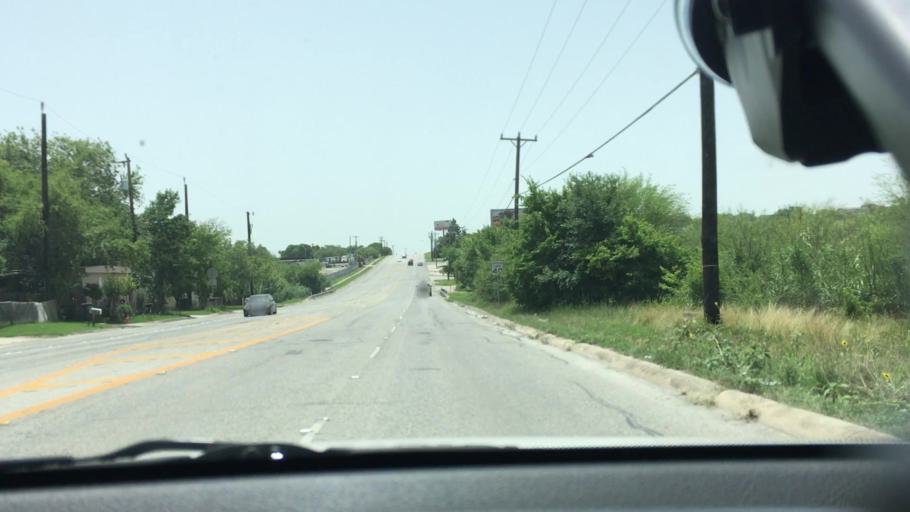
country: US
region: Texas
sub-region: Bexar County
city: Live Oak
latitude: 29.5694
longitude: -98.3562
